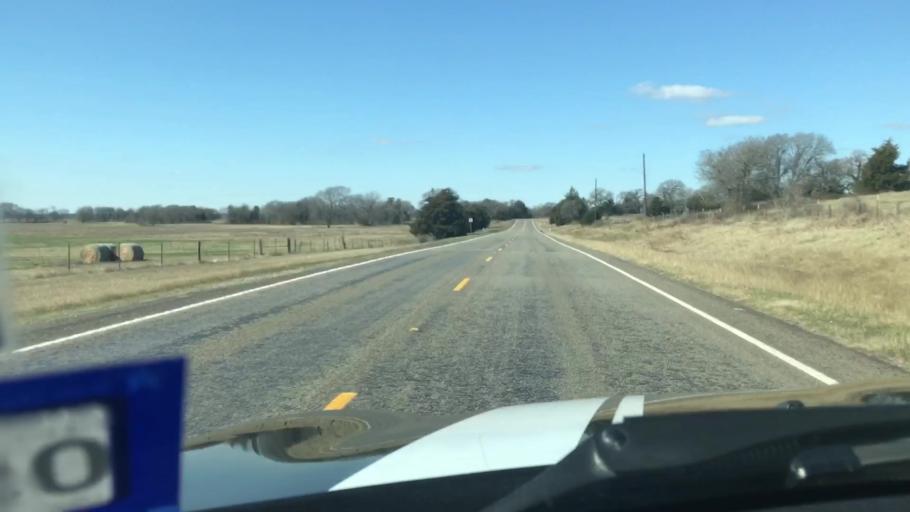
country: US
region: Texas
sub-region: Robertson County
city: Calvert
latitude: 30.8764
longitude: -96.7294
